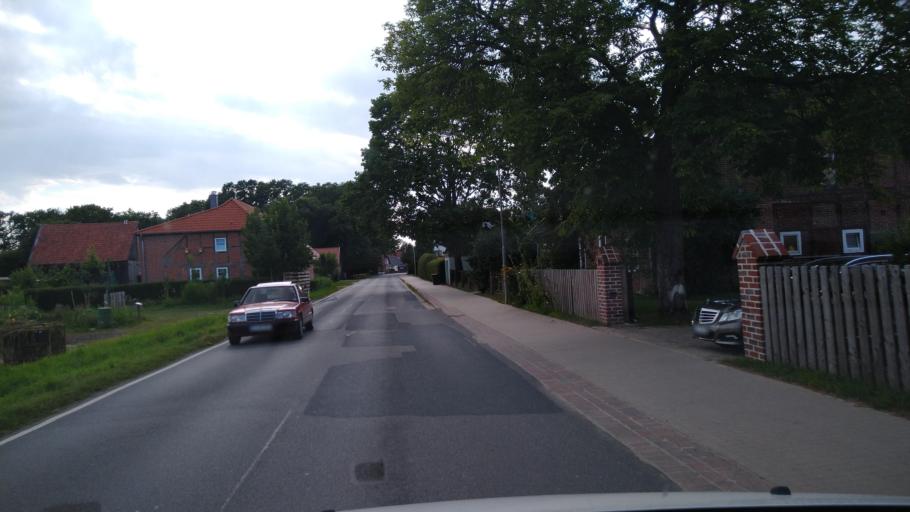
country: DE
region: Lower Saxony
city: Wienhausen
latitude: 52.5788
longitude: 10.1523
